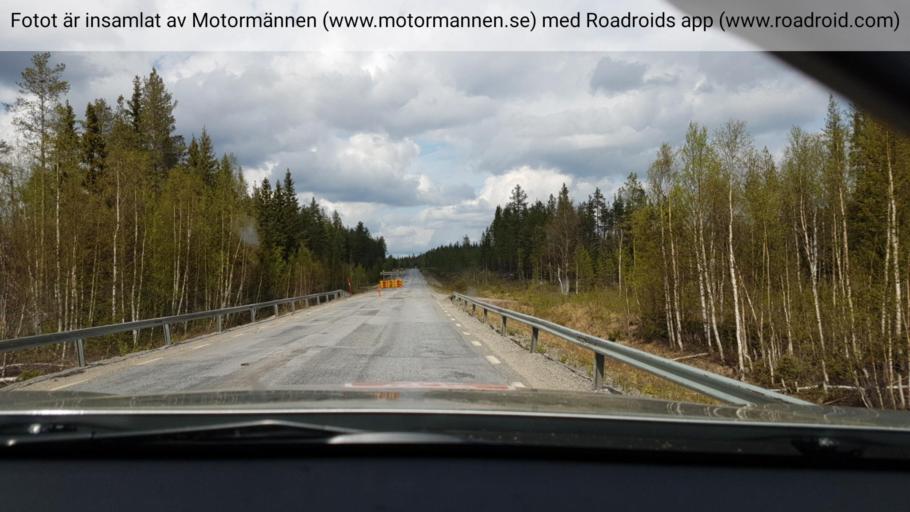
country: SE
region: Vaesternorrland
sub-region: OErnskoeldsviks Kommun
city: Bredbyn
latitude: 63.9687
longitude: 18.4983
